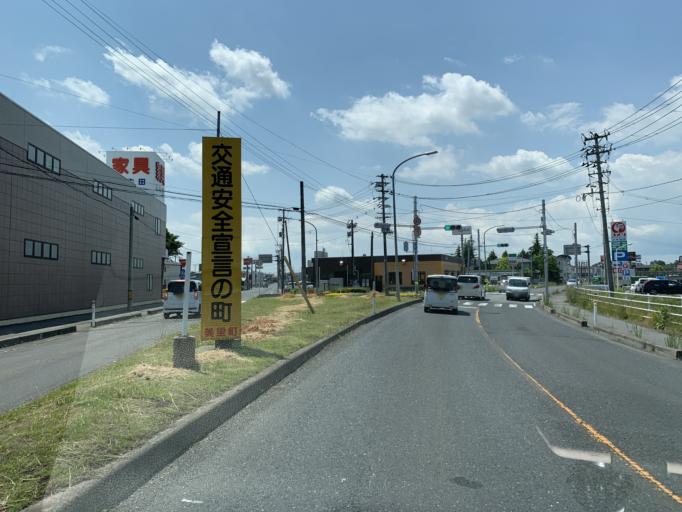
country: JP
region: Miyagi
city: Kogota
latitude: 38.5469
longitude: 141.0613
